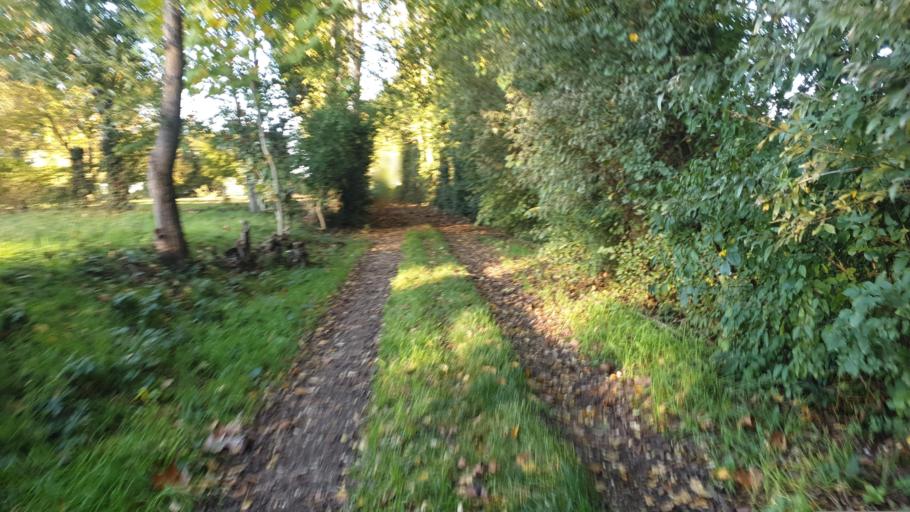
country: IT
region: Veneto
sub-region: Provincia di Venezia
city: Scaltenigo
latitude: 45.4676
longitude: 12.0862
